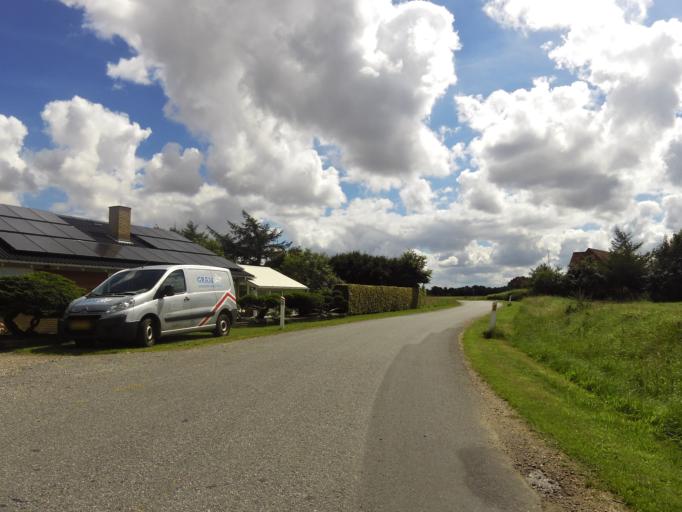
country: DK
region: South Denmark
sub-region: Haderslev Kommune
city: Vojens
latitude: 55.2812
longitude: 9.2074
